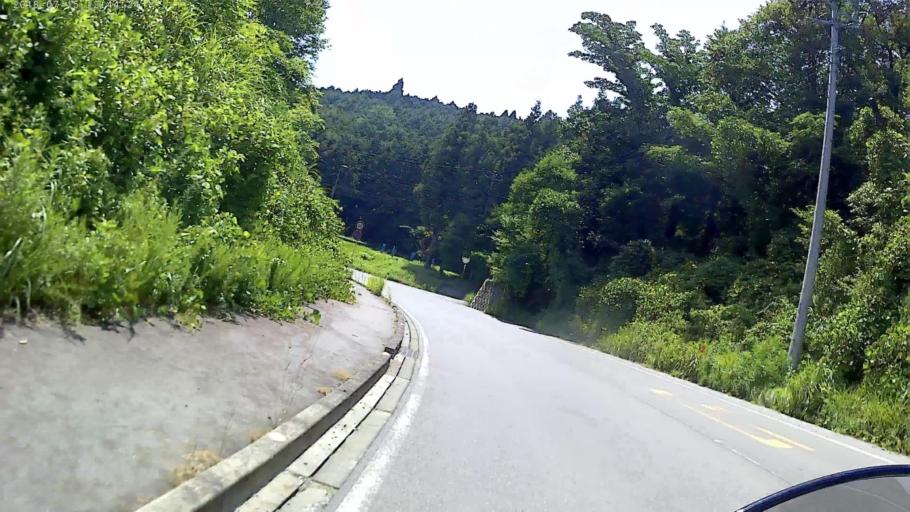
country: JP
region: Shizuoka
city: Gotemba
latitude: 35.3644
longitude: 138.9755
